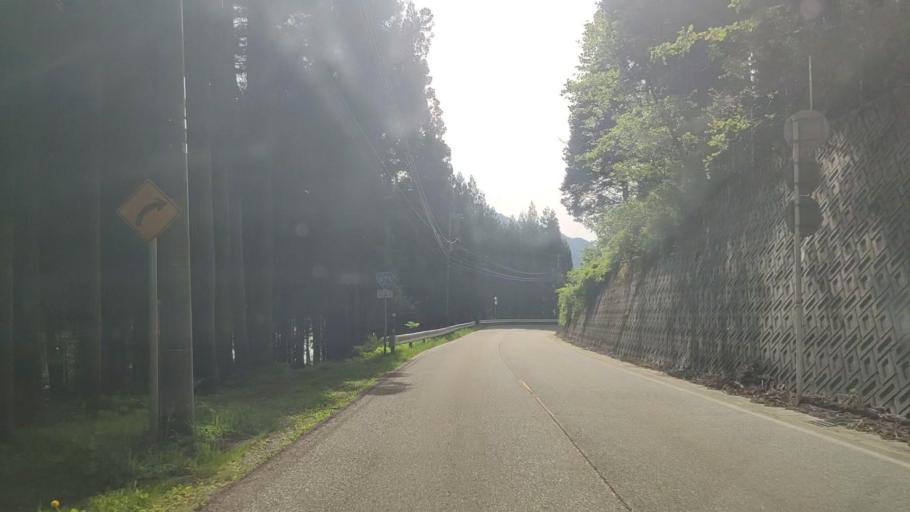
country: JP
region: Gifu
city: Takayama
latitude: 36.2976
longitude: 137.3571
